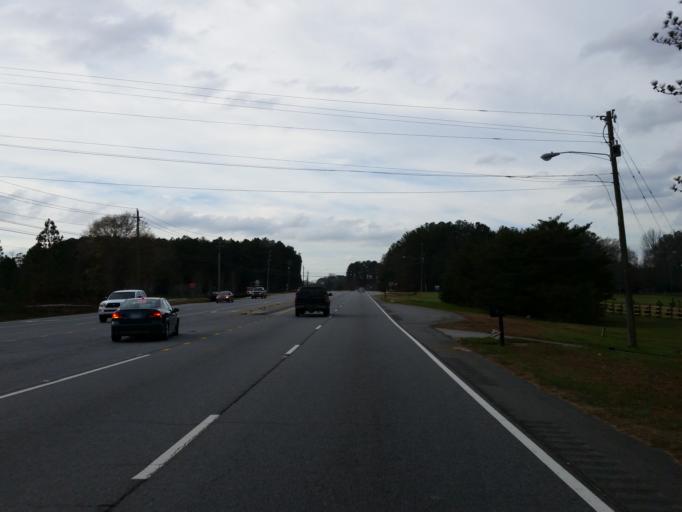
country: US
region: Georgia
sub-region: Cobb County
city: Powder Springs
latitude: 33.8987
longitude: -84.6559
